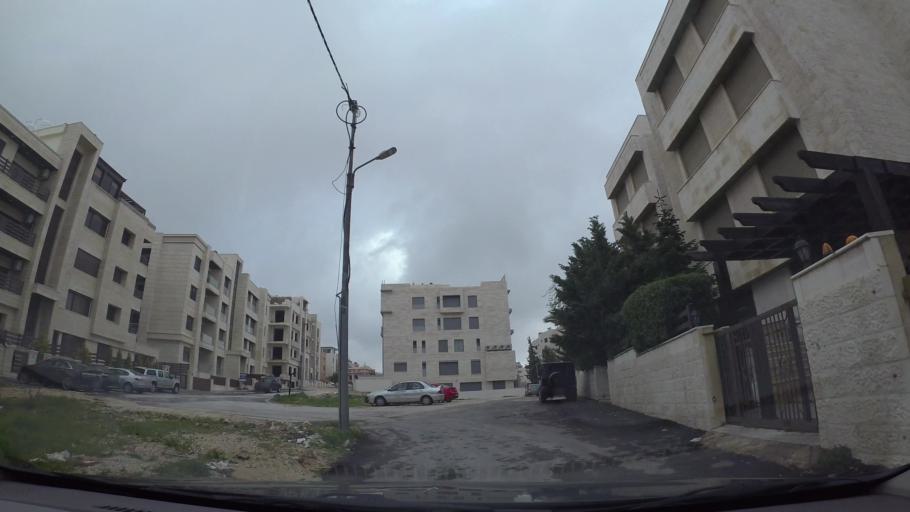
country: JO
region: Amman
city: Wadi as Sir
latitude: 31.9481
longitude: 35.8721
